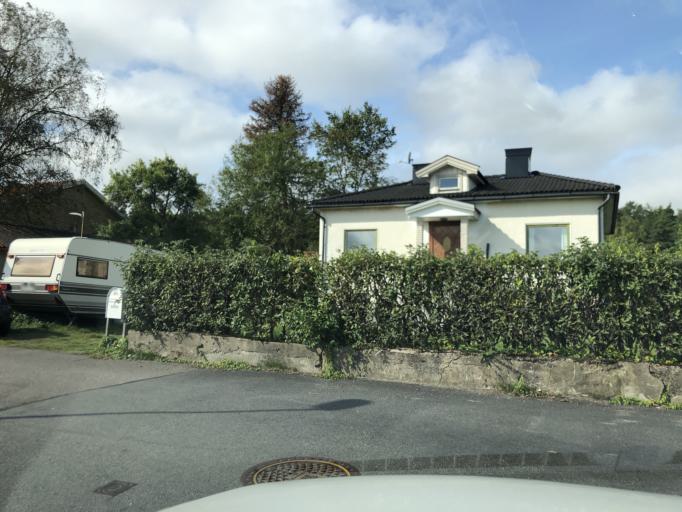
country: SE
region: Vaestra Goetaland
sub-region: Goteborg
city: Majorna
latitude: 57.7423
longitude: 11.9128
